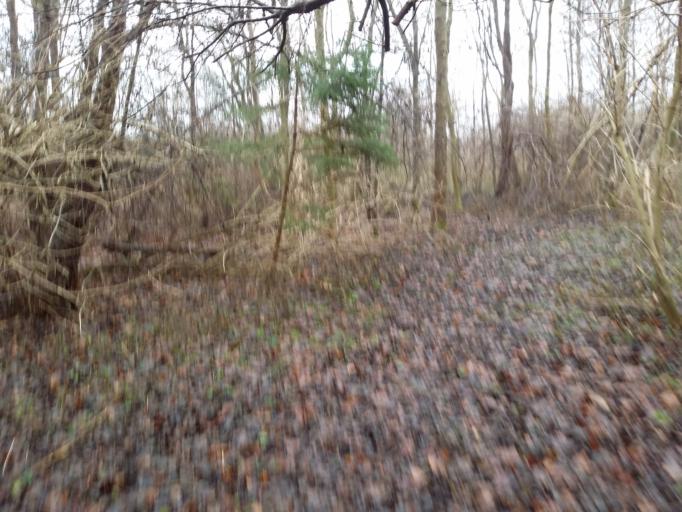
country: DK
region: Capital Region
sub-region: Frederikssund Kommune
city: Slangerup
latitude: 55.8400
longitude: 12.1922
